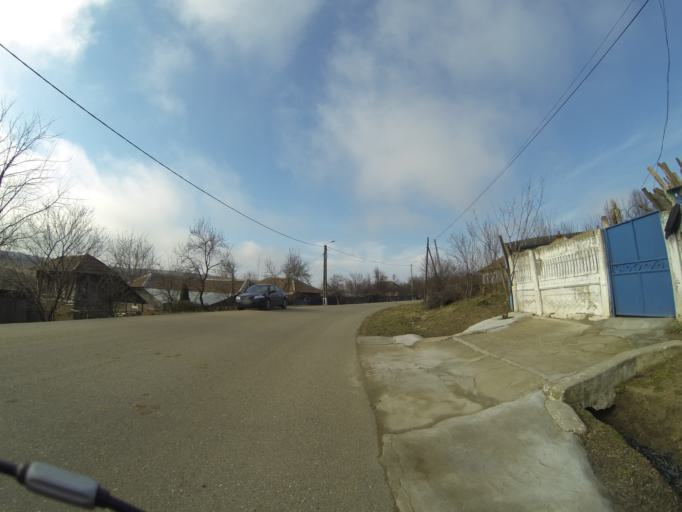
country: RO
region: Mehedinti
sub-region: Comuna Poroina Mare
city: Poroina Mare
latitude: 44.4950
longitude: 22.9885
